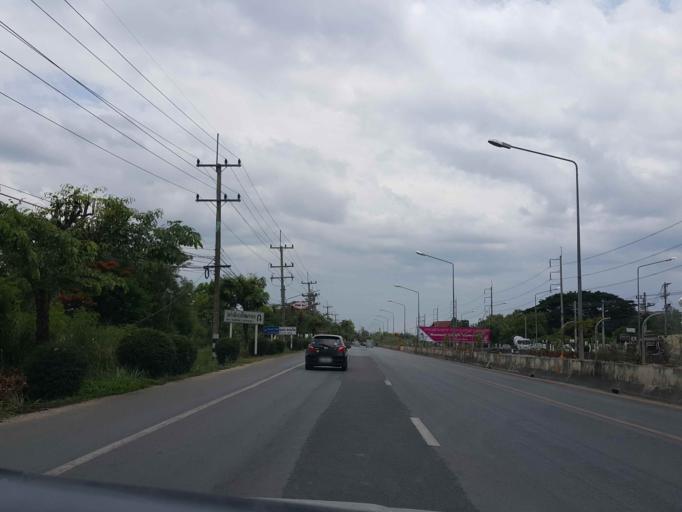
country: TH
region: Chiang Mai
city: Chiang Mai
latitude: 18.7734
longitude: 98.9516
